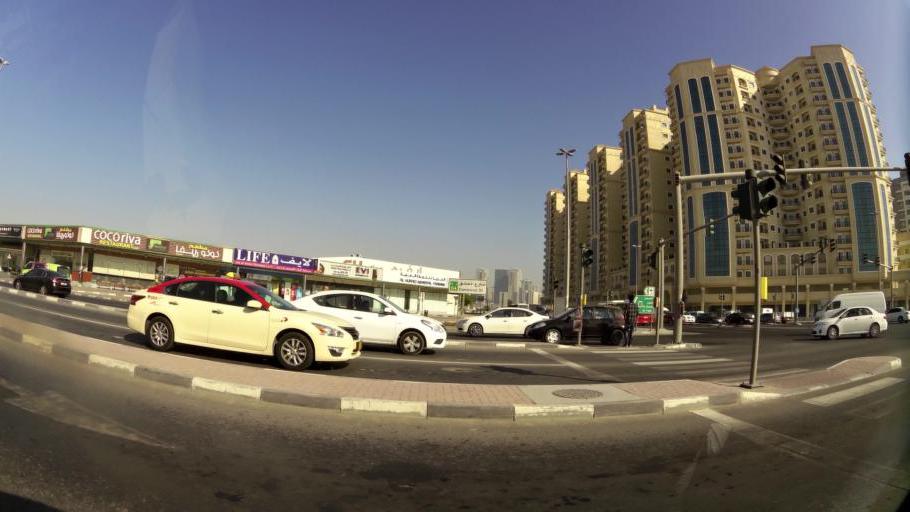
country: AE
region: Ash Shariqah
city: Sharjah
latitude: 25.2918
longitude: 55.3947
